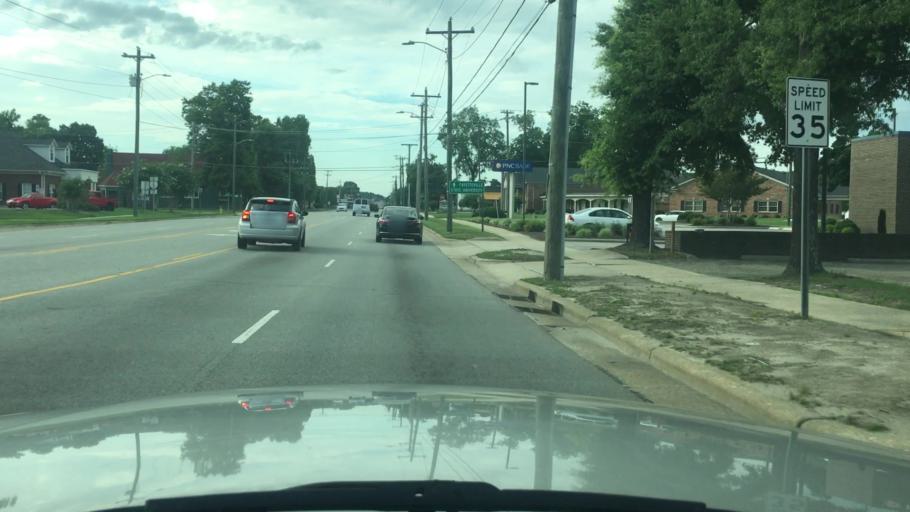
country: US
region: North Carolina
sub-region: Cumberland County
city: Fayetteville
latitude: 35.0586
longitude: -78.8769
